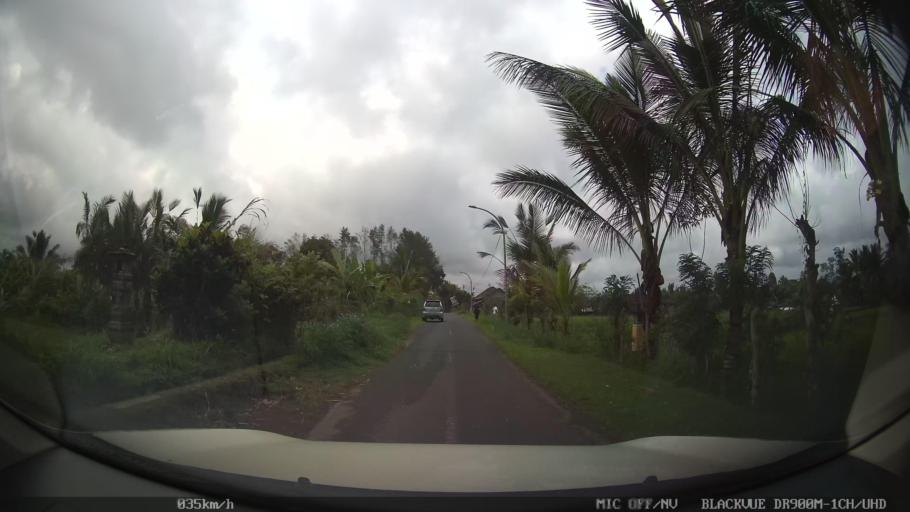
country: ID
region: Bali
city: Pemijian
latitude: -8.4385
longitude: 115.2268
